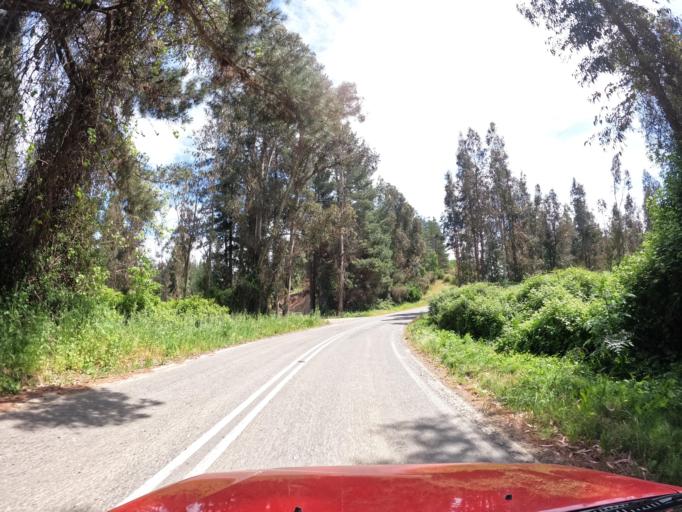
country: CL
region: Maule
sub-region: Provincia de Talca
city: Talca
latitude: -34.9953
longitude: -71.8790
